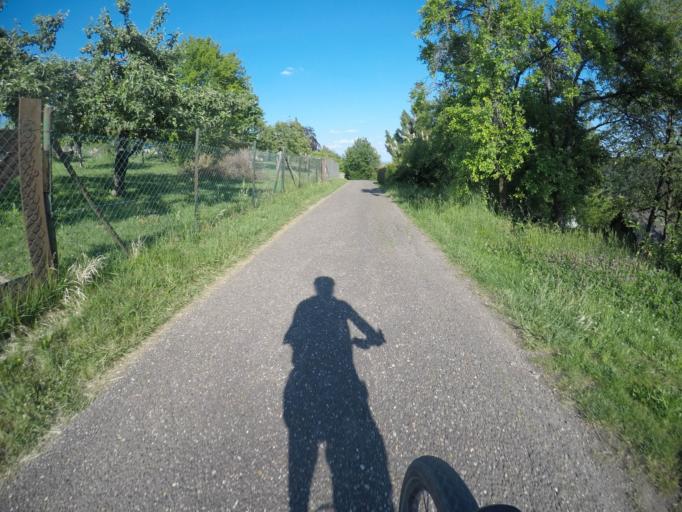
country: DE
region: Baden-Wuerttemberg
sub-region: Regierungsbezirk Stuttgart
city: Ostfildern
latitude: 48.7394
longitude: 9.2622
